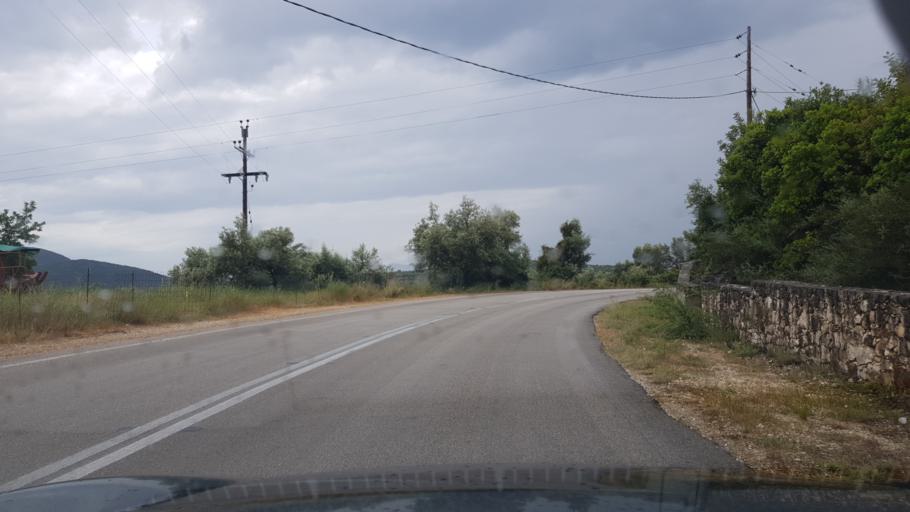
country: GR
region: Ionian Islands
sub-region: Lefkada
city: Nidri
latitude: 38.6478
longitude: 20.6764
